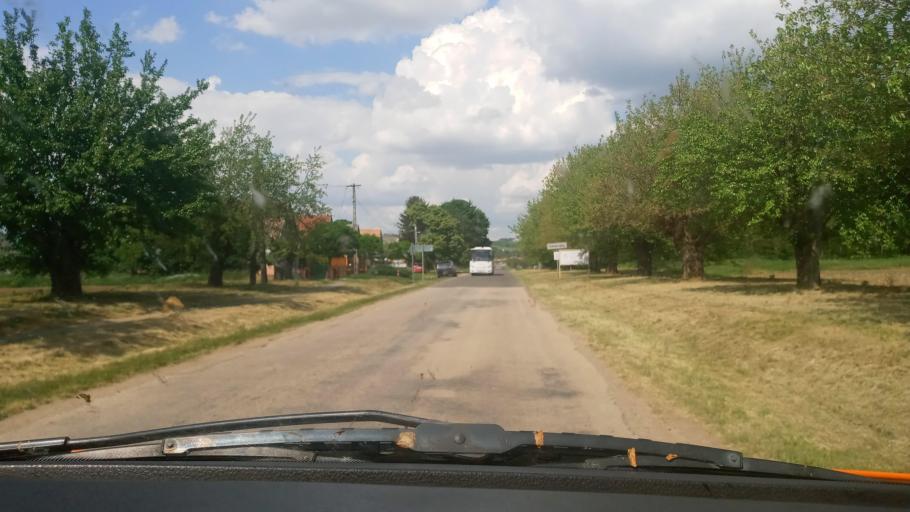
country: HU
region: Baranya
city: Siklos
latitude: 45.8538
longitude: 18.3604
